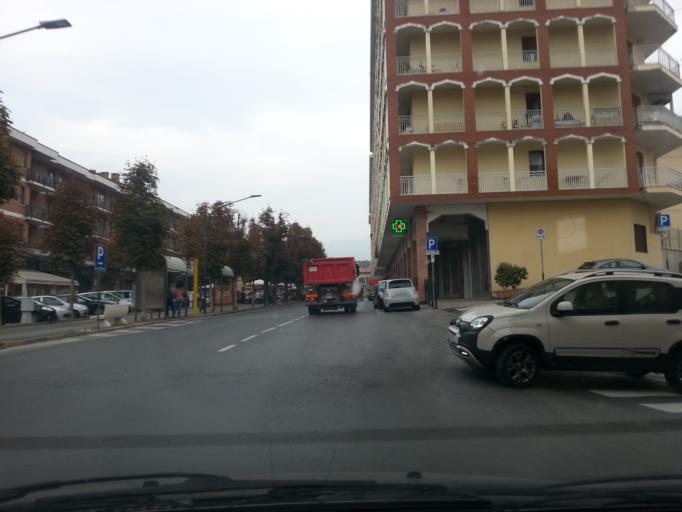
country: IT
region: Piedmont
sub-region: Provincia di Torino
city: Giaveno
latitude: 45.0405
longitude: 7.3549
